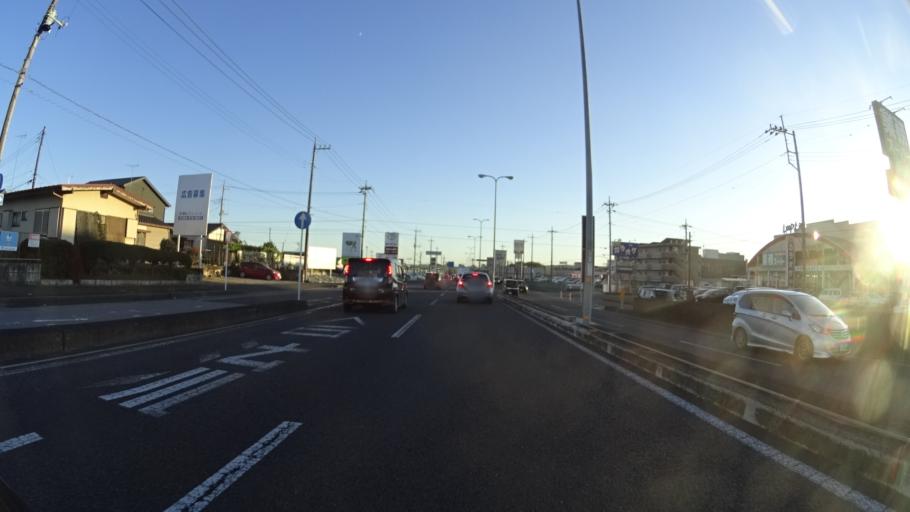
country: JP
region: Tochigi
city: Utsunomiya-shi
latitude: 36.5476
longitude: 139.8496
